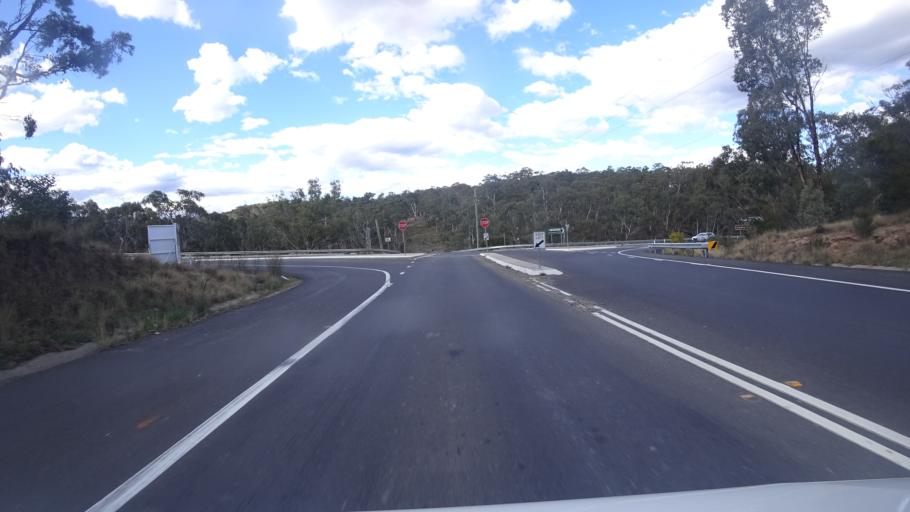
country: AU
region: New South Wales
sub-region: Lithgow
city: Bowenfels
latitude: -33.5427
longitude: 150.1667
